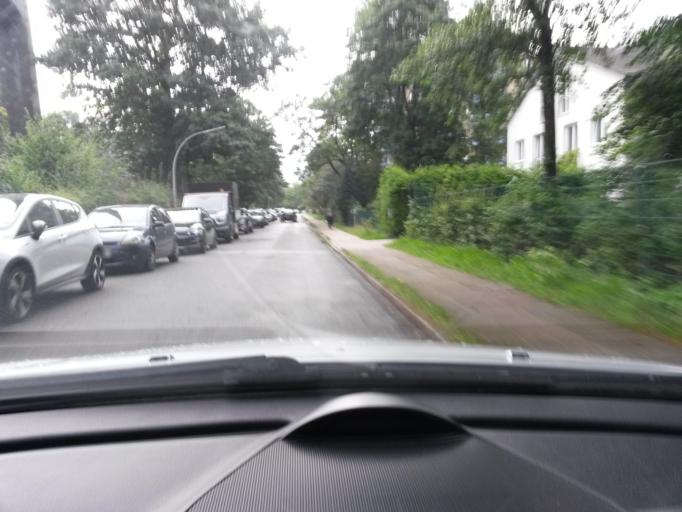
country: DE
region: Schleswig-Holstein
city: Barsbuettel
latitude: 53.5874
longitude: 10.1488
